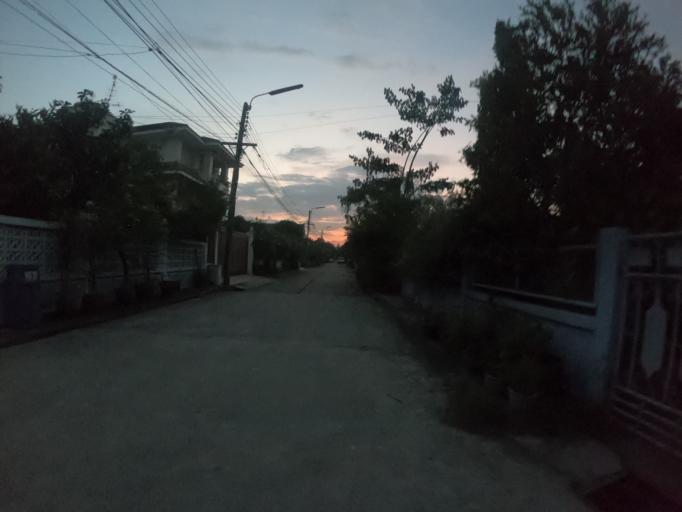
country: TH
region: Bangkok
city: Lat Phrao
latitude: 13.8279
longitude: 100.6132
